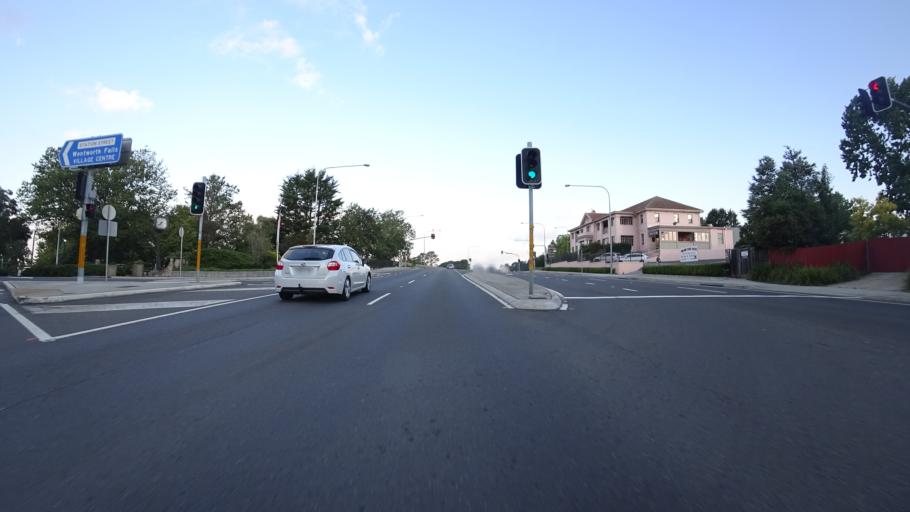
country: AU
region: New South Wales
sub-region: Blue Mountains Municipality
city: Leura
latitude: -33.7104
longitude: 150.3756
